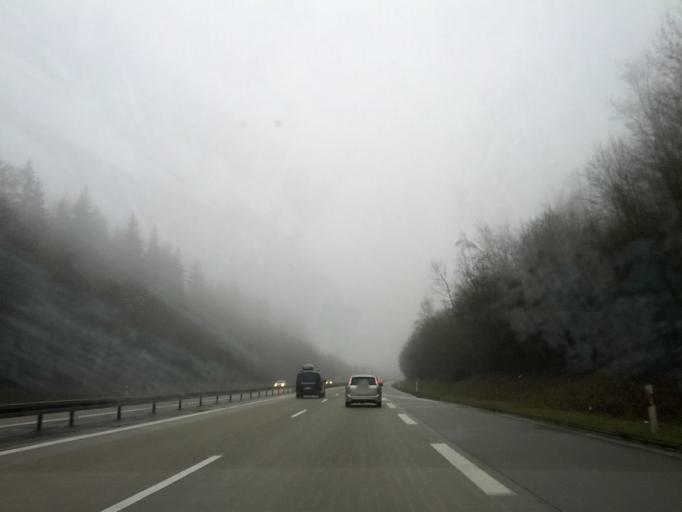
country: DE
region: Baden-Wuerttemberg
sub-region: Regierungsbezirk Stuttgart
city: Nattheim
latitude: 48.7440
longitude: 10.1967
